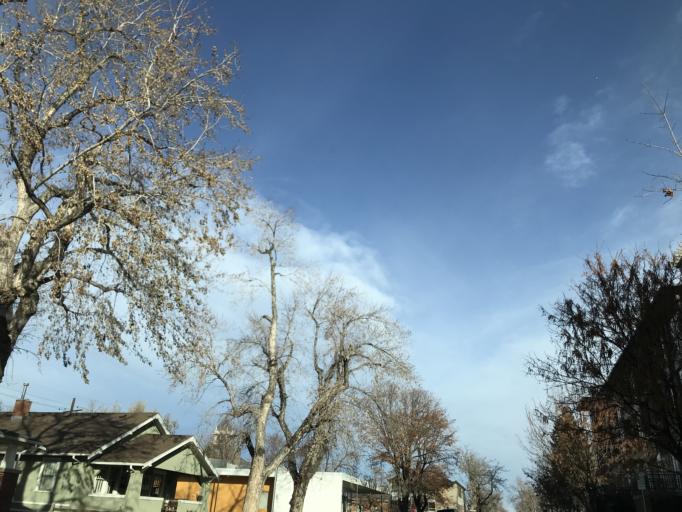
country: US
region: Colorado
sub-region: Arapahoe County
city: Littleton
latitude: 39.6124
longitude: -105.0115
